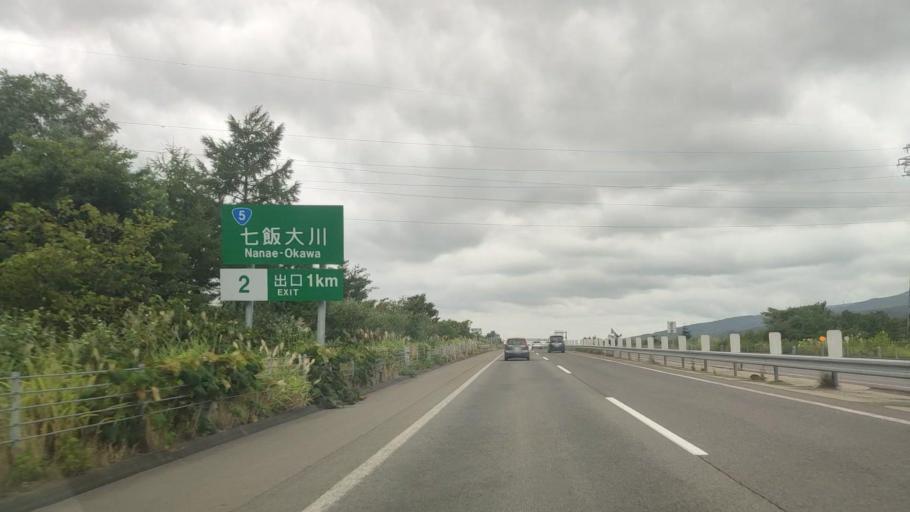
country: JP
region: Hokkaido
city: Nanae
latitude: 41.8581
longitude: 140.7359
